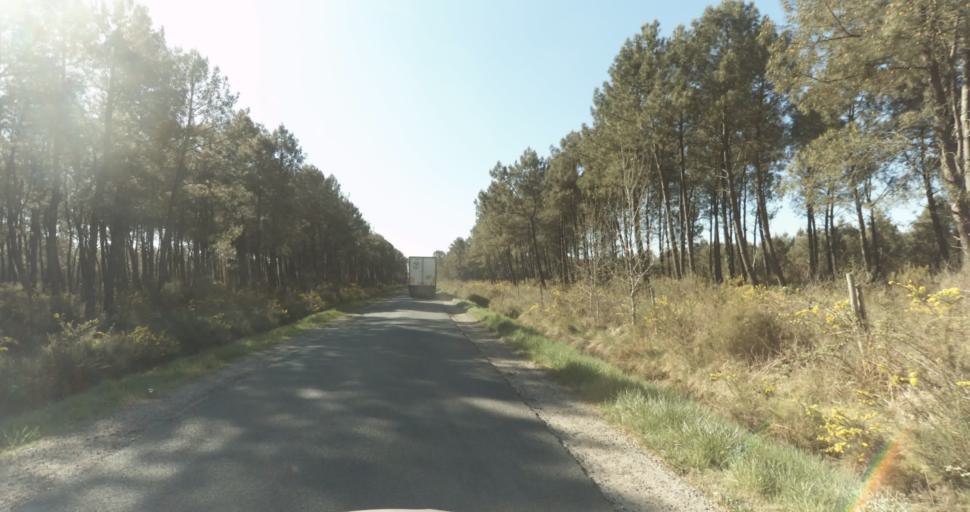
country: FR
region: Aquitaine
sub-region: Departement de la Gironde
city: Marcheprime
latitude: 44.7587
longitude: -0.8517
